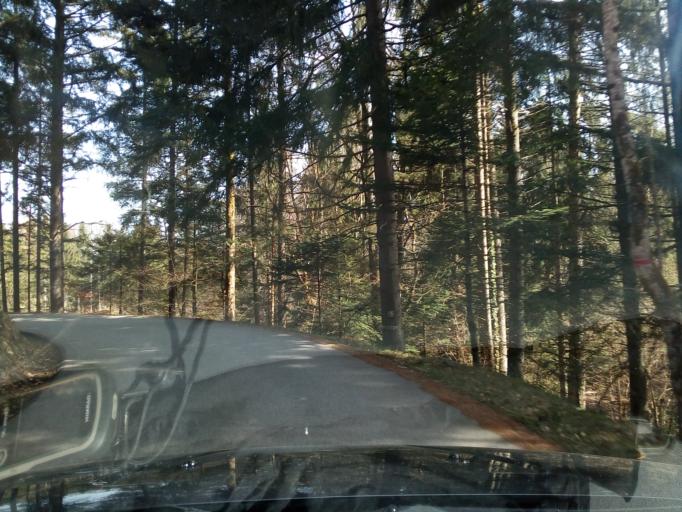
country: FR
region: Rhone-Alpes
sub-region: Departement de l'Isere
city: Revel
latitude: 45.1613
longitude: 5.8785
